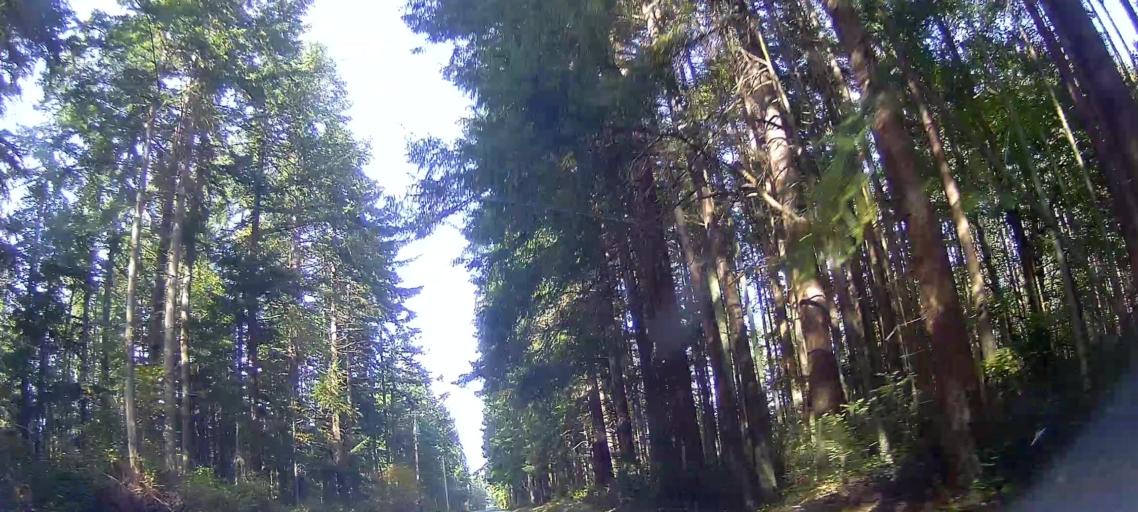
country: US
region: Washington
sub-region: Island County
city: Camano
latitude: 48.2112
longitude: -122.4561
